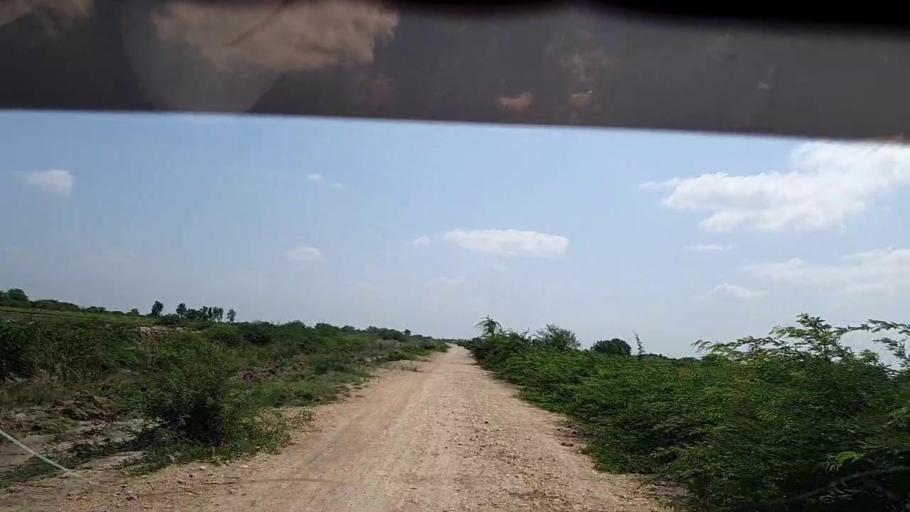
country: PK
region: Sindh
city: Kadhan
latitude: 24.5967
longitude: 68.9916
